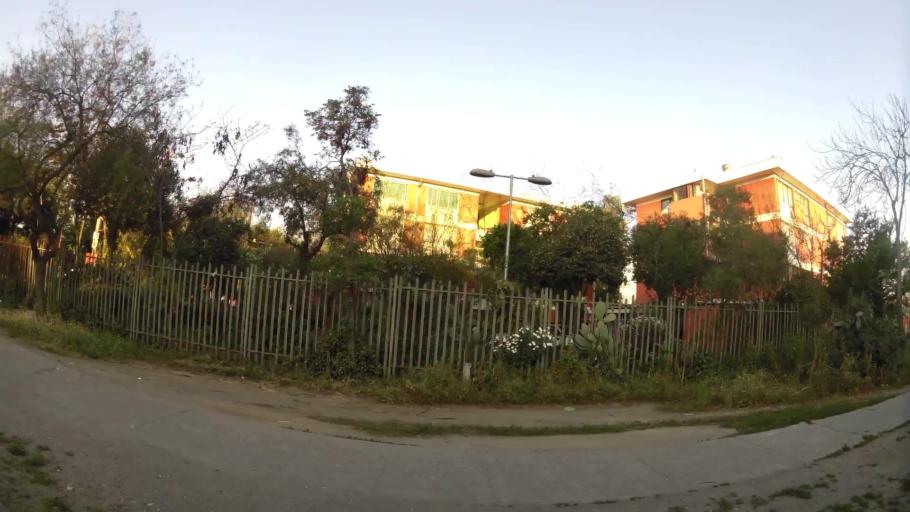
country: CL
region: Santiago Metropolitan
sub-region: Provincia de Santiago
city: Santiago
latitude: -33.5077
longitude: -70.6289
